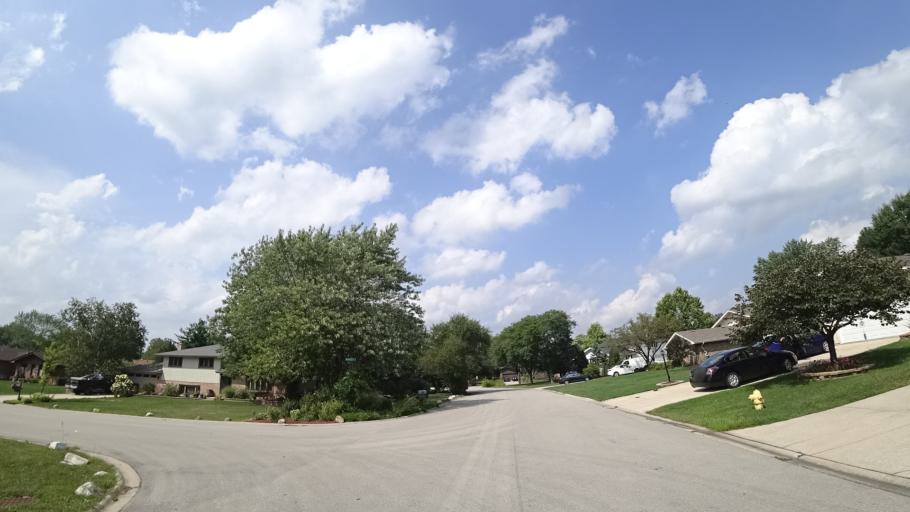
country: US
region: Illinois
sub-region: Will County
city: Goodings Grove
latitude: 41.6426
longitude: -87.9135
